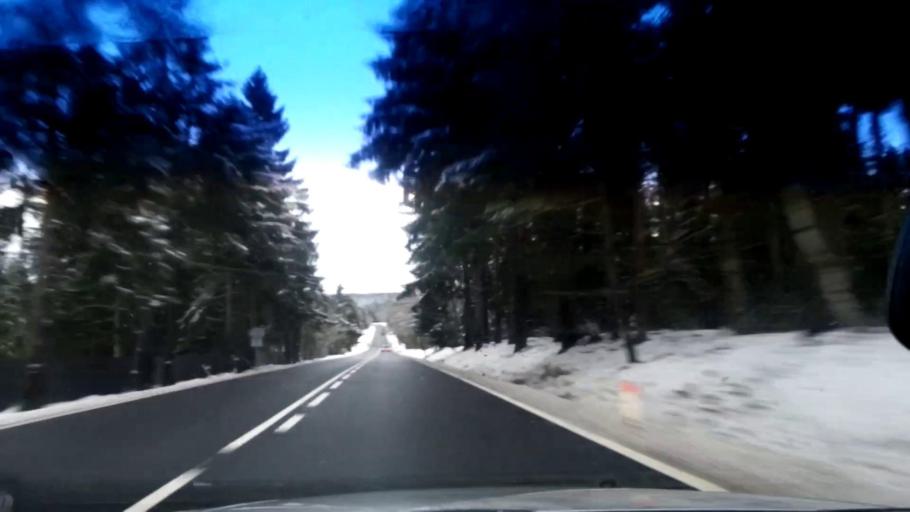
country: CZ
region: Karlovarsky
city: Hazlov
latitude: 50.1831
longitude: 12.2452
